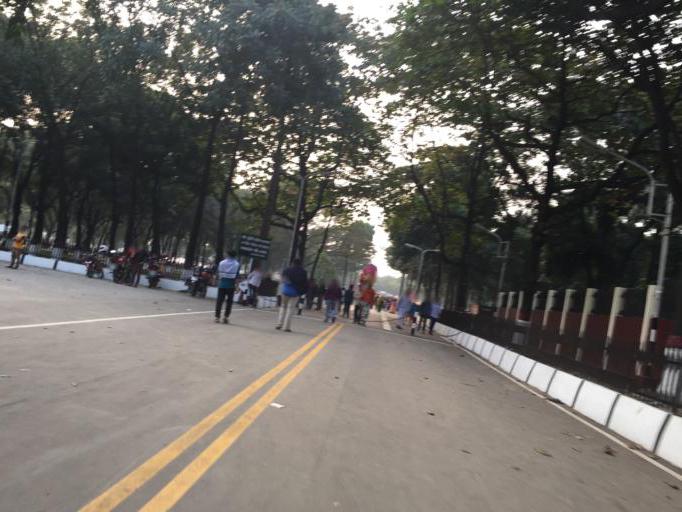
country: BD
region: Dhaka
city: Azimpur
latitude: 23.7938
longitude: 90.3476
